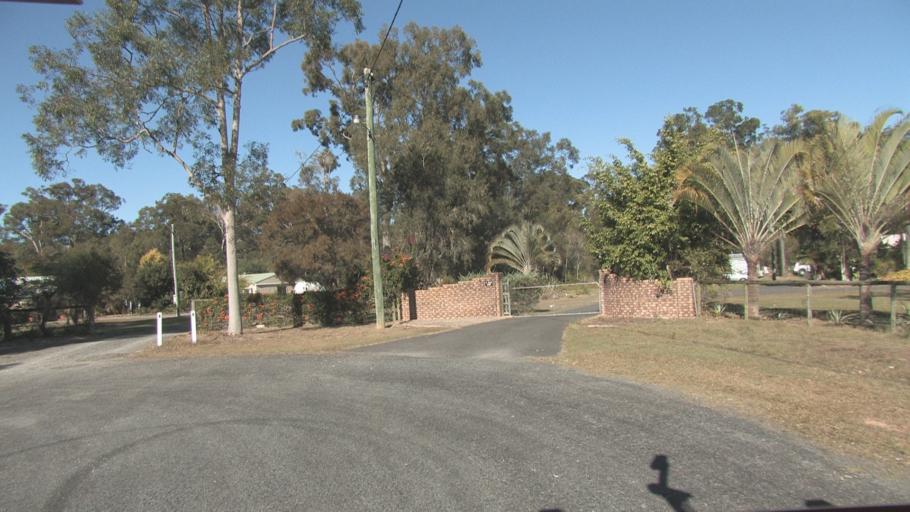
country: AU
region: Queensland
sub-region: Logan
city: Chambers Flat
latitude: -27.7871
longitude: 153.1260
